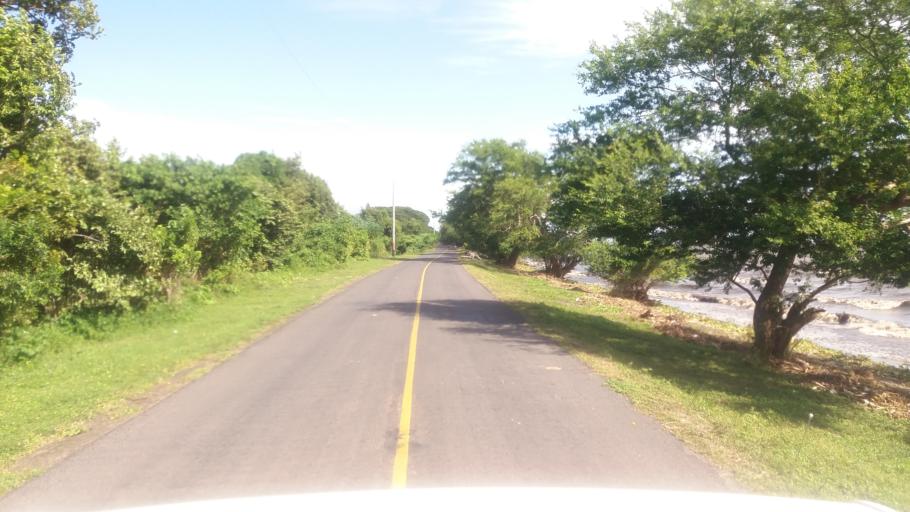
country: NI
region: Granada
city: Granada
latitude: 11.9744
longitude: -85.9425
